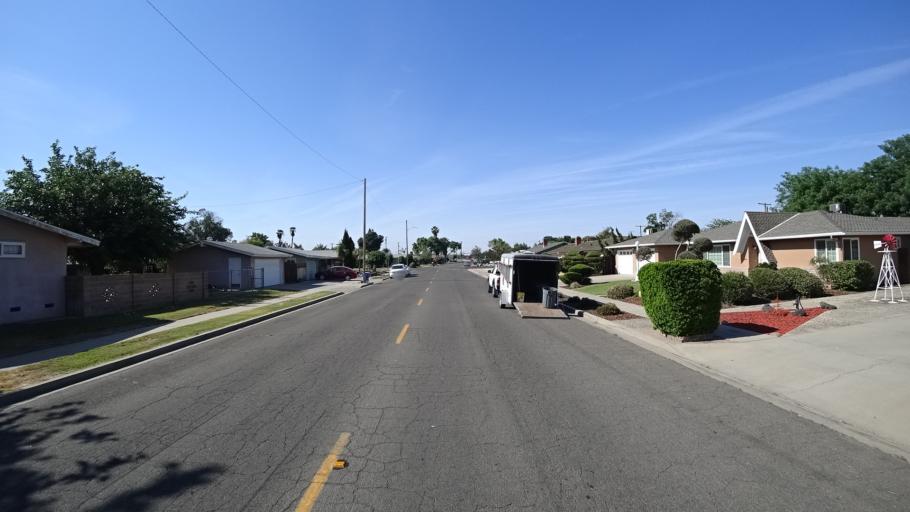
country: US
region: California
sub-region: Kings County
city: Hanford
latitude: 36.3338
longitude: -119.6318
